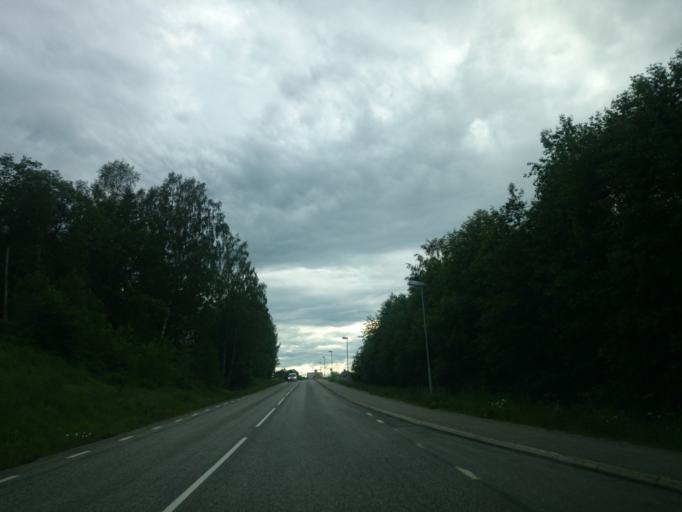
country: SE
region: Vaesternorrland
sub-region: Timra Kommun
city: Timra
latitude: 62.4667
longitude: 17.2750
